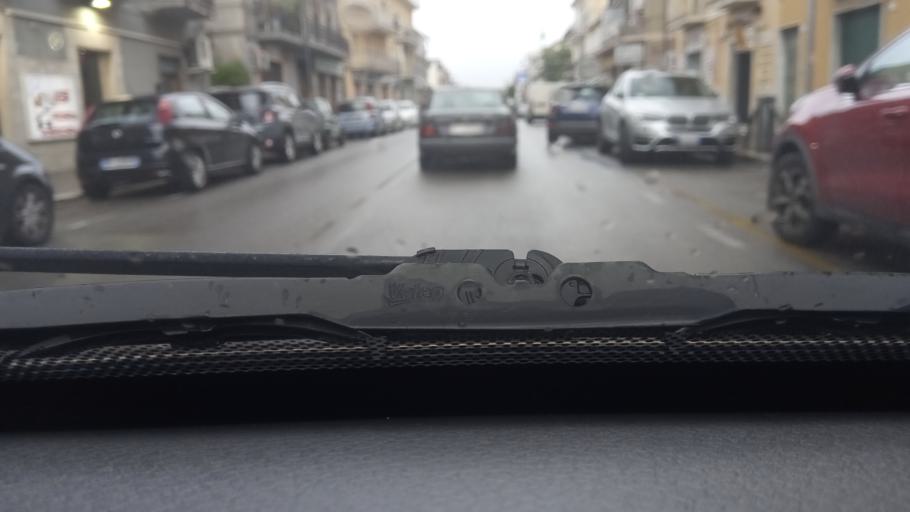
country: IT
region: Latium
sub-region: Provincia di Latina
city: Minturno
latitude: 41.2558
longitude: 13.7114
